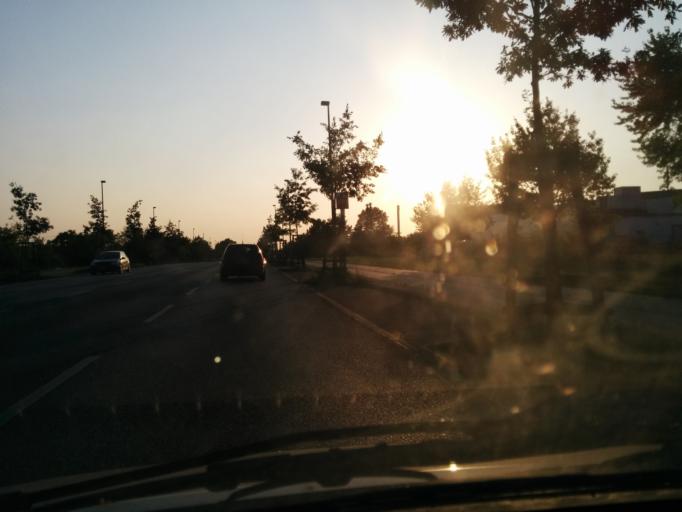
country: DE
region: Berlin
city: Altglienicke
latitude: 52.4261
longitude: 13.5346
